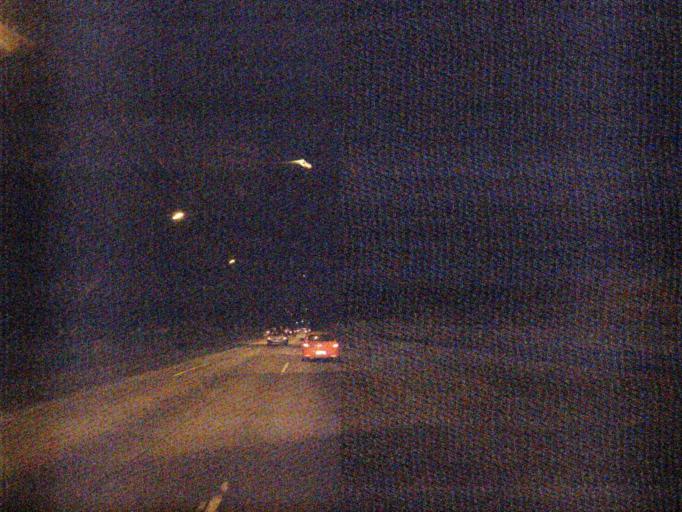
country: BR
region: Rio de Janeiro
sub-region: Rio De Janeiro
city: Rio de Janeiro
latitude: -22.9365
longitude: -43.2073
